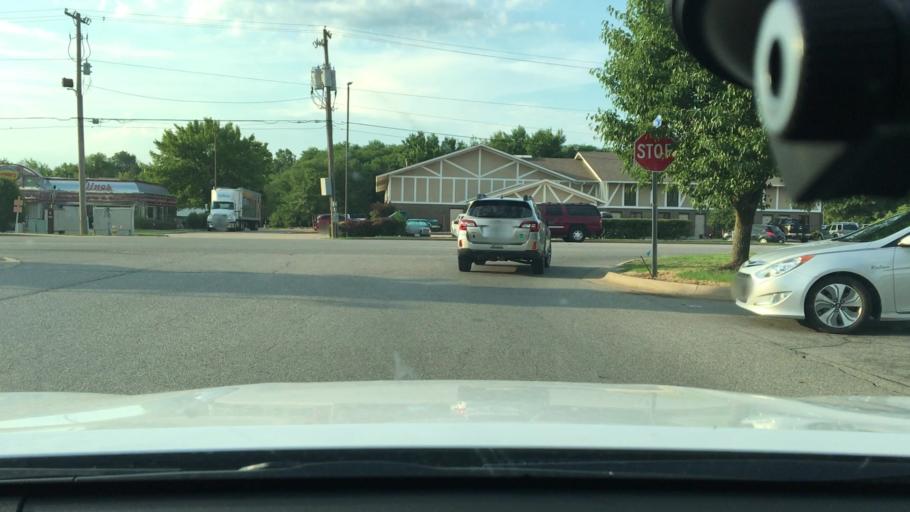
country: US
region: Arkansas
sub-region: Benton County
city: Bentonville
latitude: 36.3348
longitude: -94.1876
